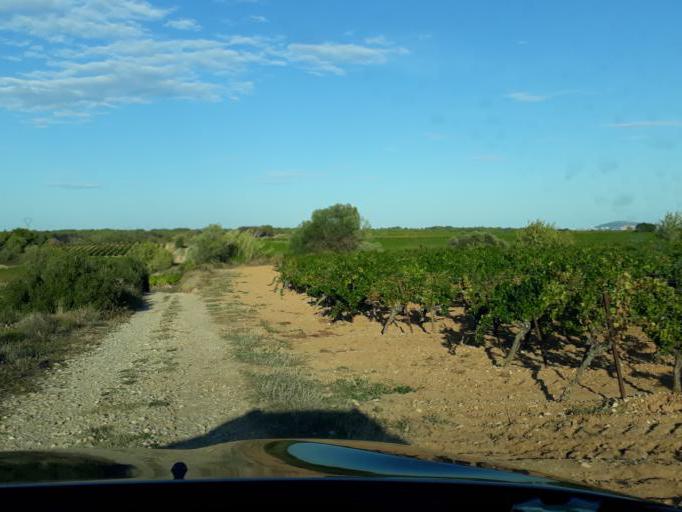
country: FR
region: Languedoc-Roussillon
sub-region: Departement de l'Herault
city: Pinet
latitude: 43.4160
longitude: 3.4884
